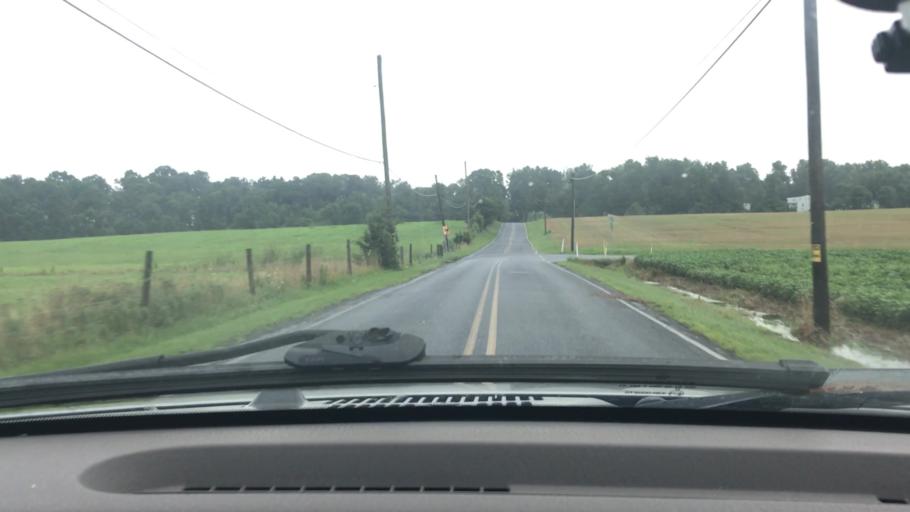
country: US
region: Pennsylvania
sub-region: Lancaster County
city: Elizabethtown
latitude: 40.2177
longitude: -76.6244
